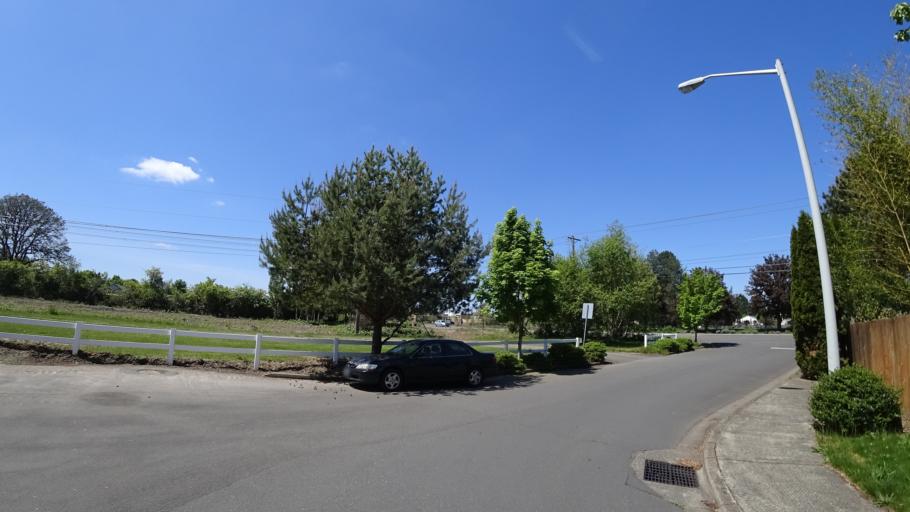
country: US
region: Oregon
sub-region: Washington County
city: Aloha
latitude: 45.5148
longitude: -122.8955
